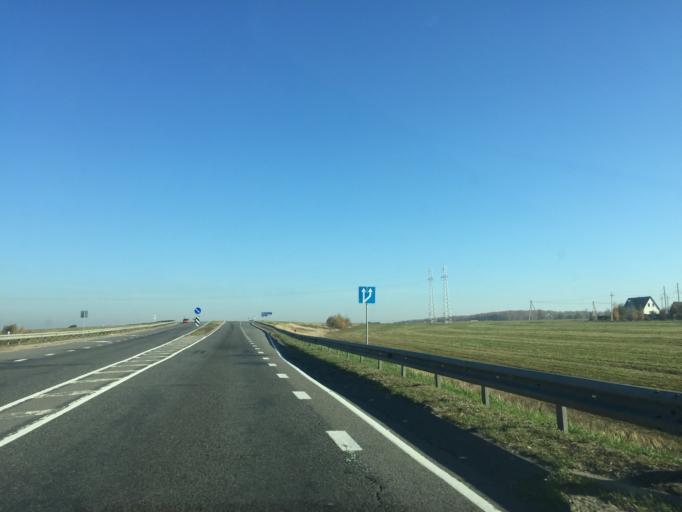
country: BY
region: Mogilev
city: Buynichy
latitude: 53.9452
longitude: 30.2176
